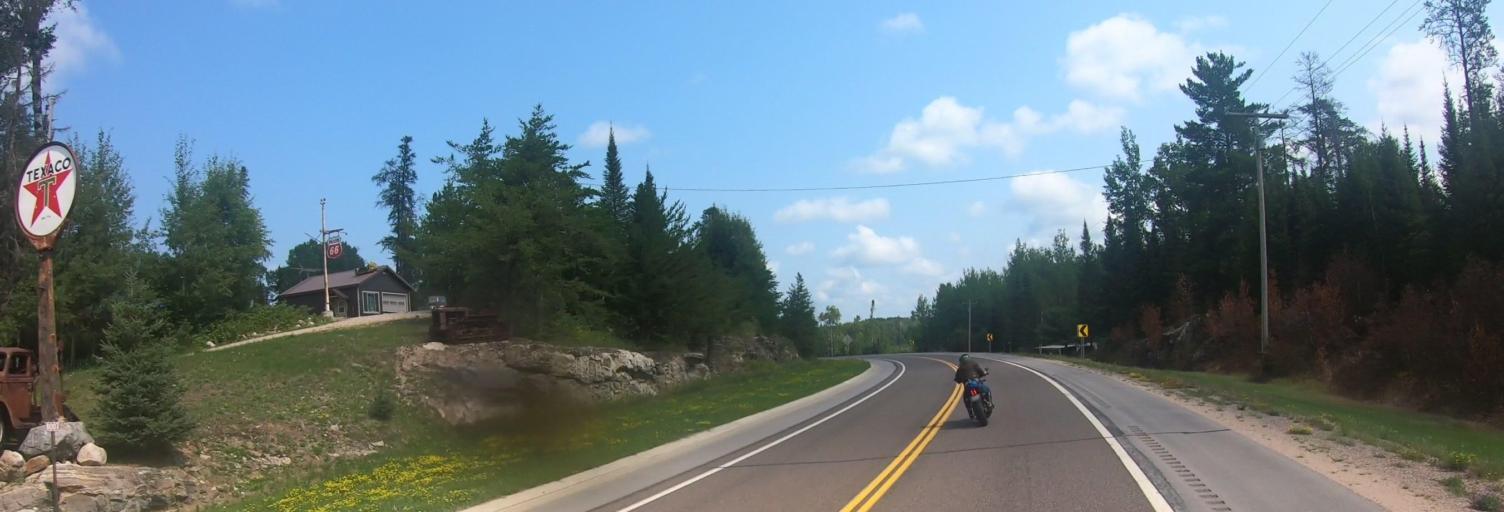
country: US
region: Minnesota
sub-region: Saint Louis County
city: Parkville
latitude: 48.1104
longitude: -92.5479
